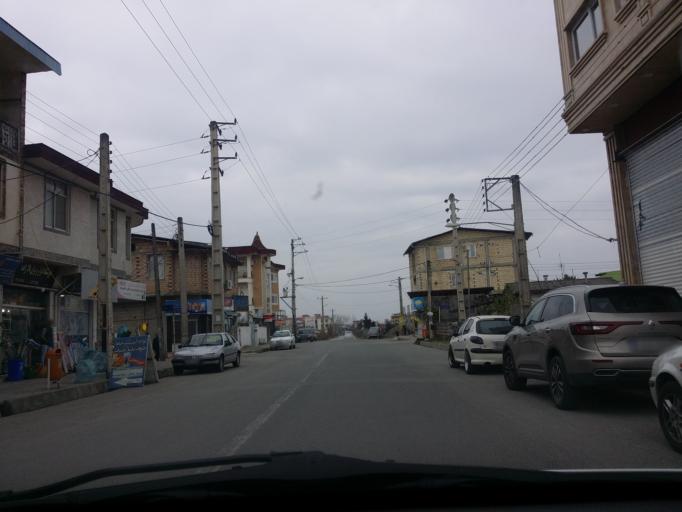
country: IR
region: Mazandaran
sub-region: Nowshahr
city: Nowshahr
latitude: 36.6430
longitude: 51.4851
